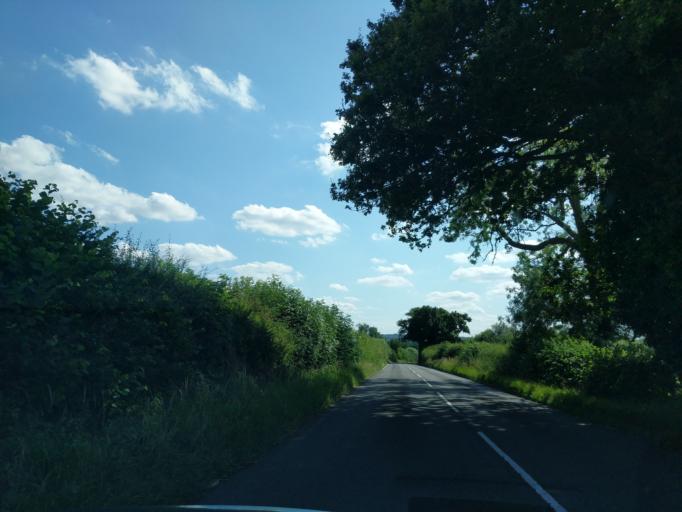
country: GB
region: England
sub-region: Staffordshire
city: Rugeley
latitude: 52.7942
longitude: -1.9337
